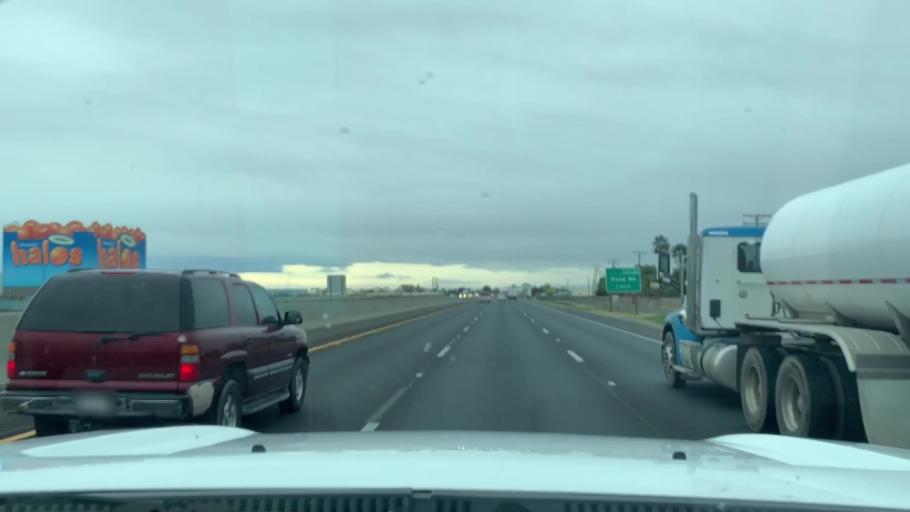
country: US
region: California
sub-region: Kern County
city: Delano
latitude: 35.7363
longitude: -119.2408
